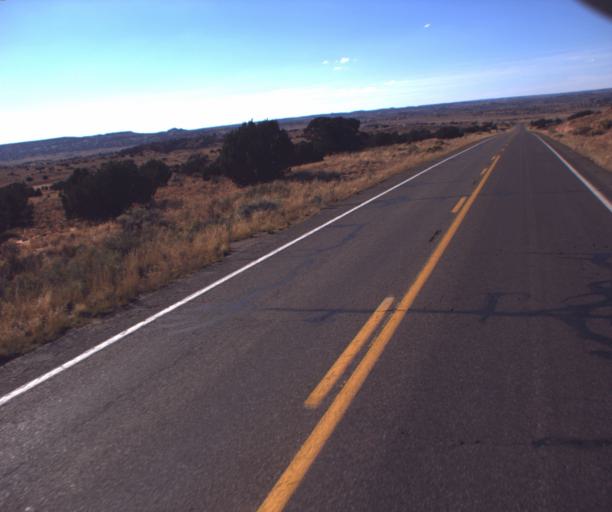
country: US
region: Arizona
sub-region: Coconino County
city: Kaibito
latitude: 36.5769
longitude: -111.1262
